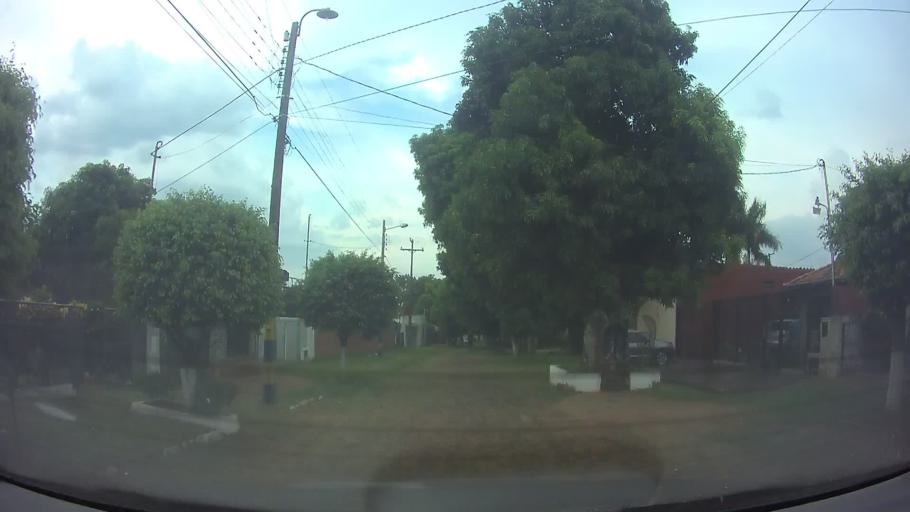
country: PY
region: Central
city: San Lorenzo
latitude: -25.2821
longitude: -57.4936
